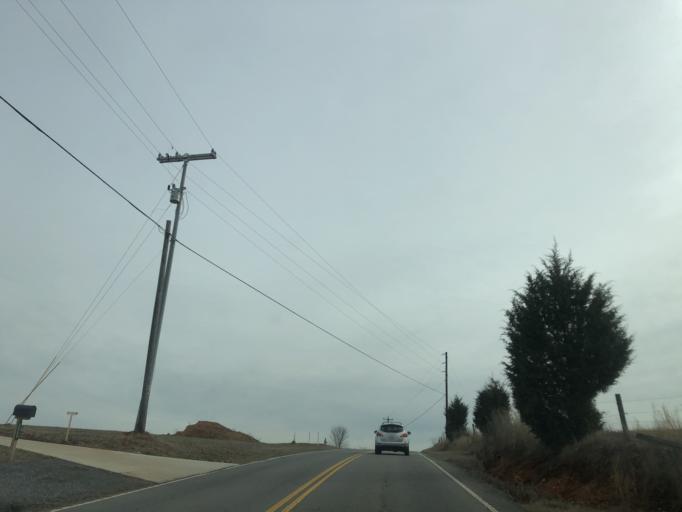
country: US
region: Tennessee
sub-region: Sumner County
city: White House
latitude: 36.4829
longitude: -86.5789
